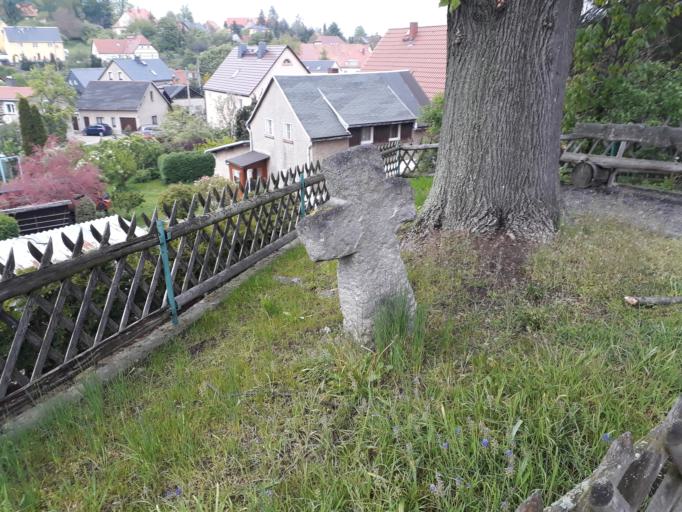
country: DE
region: Saxony
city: Reinhardtsgrimma
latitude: 50.8911
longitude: 13.7524
